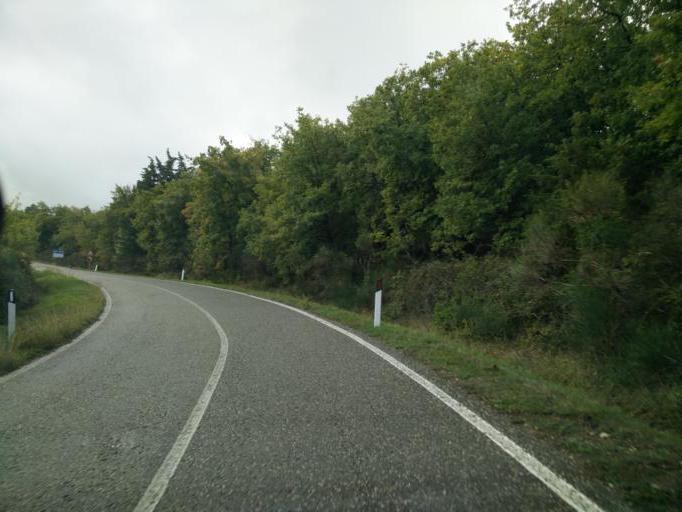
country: IT
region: Tuscany
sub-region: Province of Florence
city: Sambuca
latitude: 43.5918
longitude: 11.2604
